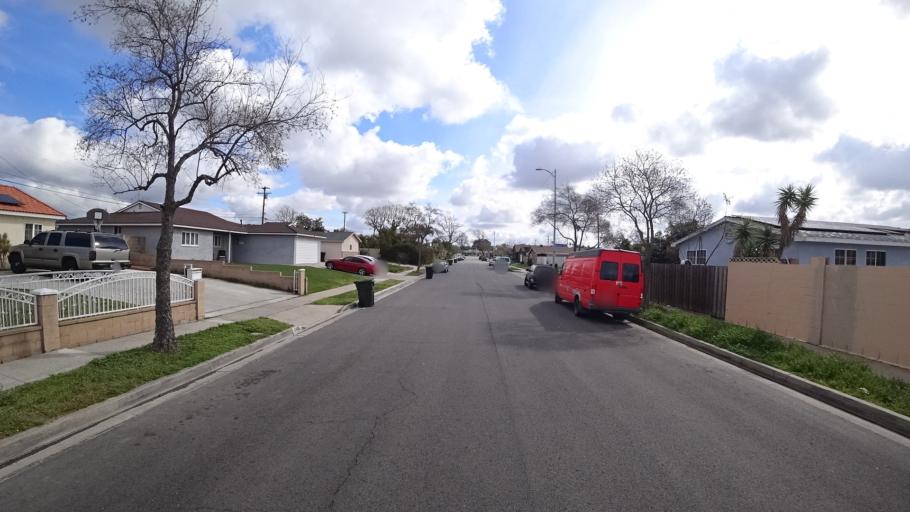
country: US
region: California
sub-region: Orange County
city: Buena Park
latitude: 33.8432
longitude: -117.9714
